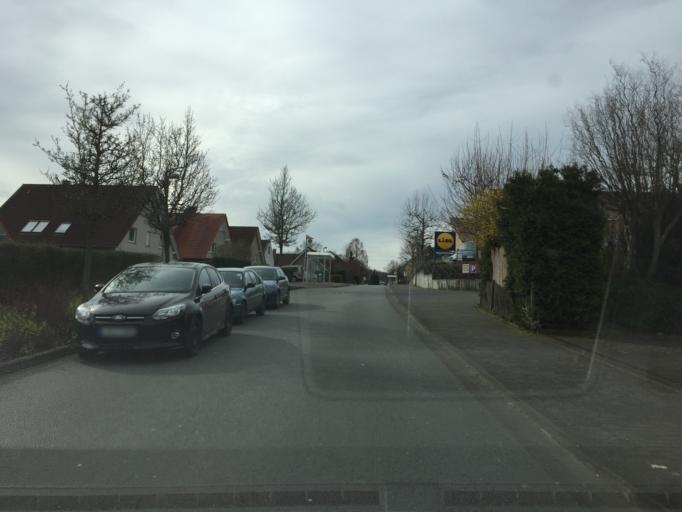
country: DE
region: North Rhine-Westphalia
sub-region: Regierungsbezirk Detmold
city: Detmold
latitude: 51.9452
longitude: 8.8350
